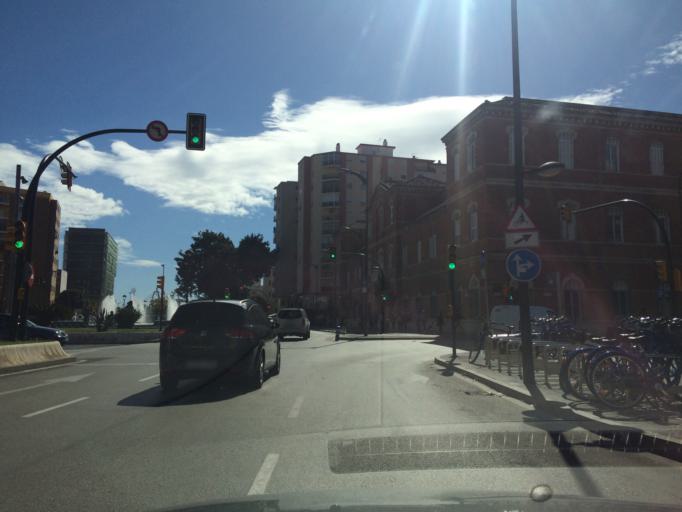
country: ES
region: Andalusia
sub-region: Provincia de Malaga
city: Malaga
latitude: 36.7119
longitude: -4.4308
